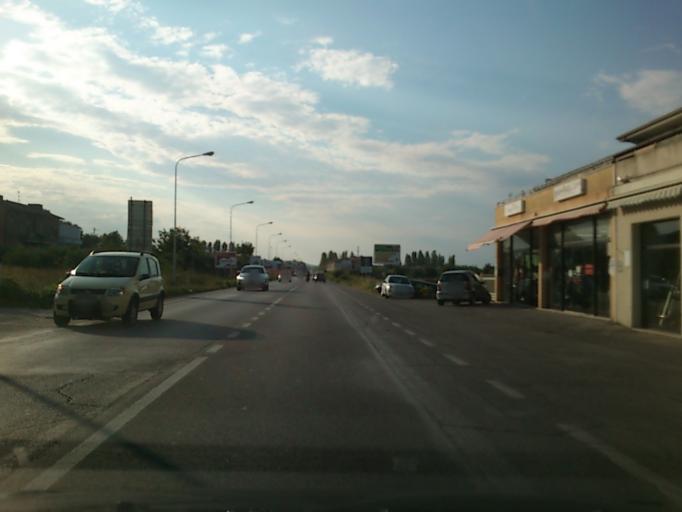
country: IT
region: The Marches
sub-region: Provincia di Pesaro e Urbino
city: Fano
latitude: 43.8328
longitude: 13.0423
